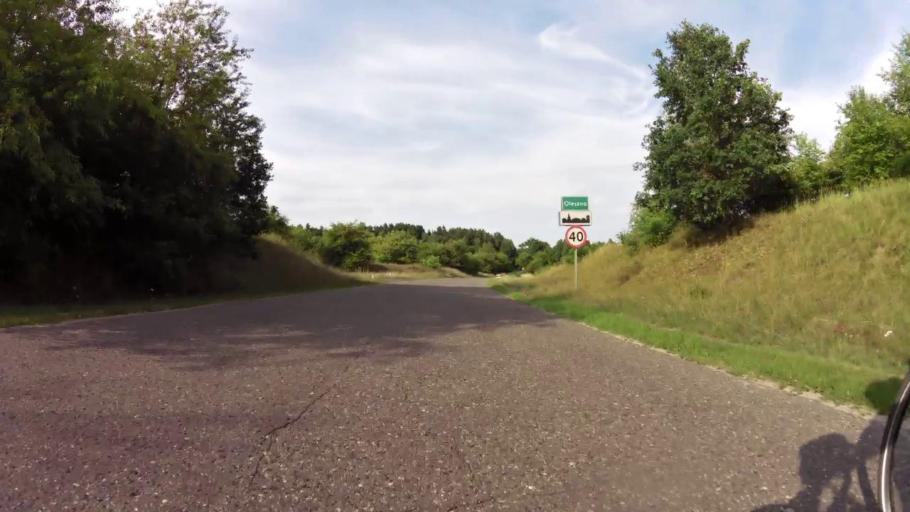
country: PL
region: West Pomeranian Voivodeship
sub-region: Powiat drawski
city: Drawsko Pomorskie
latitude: 53.4693
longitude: 15.7533
